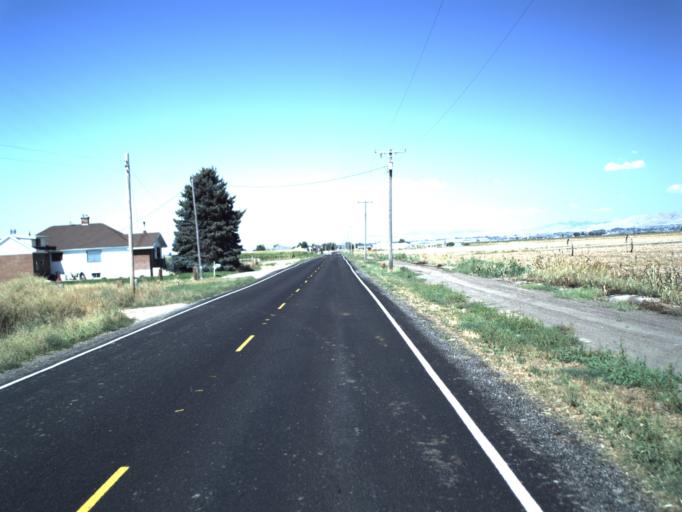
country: US
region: Utah
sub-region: Cache County
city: Lewiston
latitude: 41.9818
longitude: -111.8763
